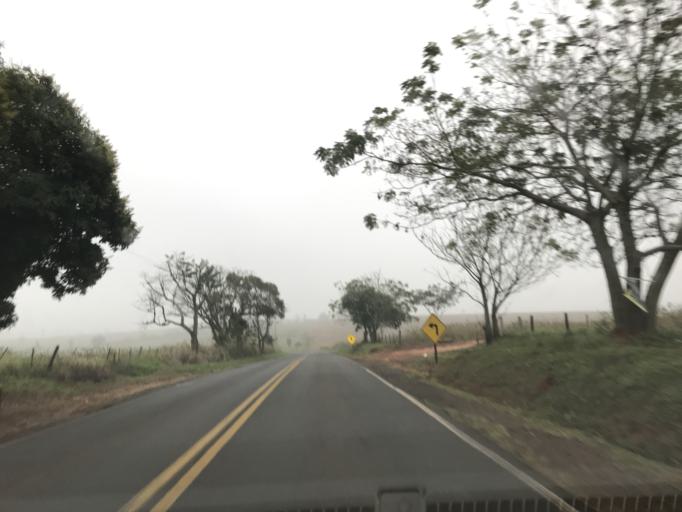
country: PY
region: Canindeyu
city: Salto del Guaira
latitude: -24.0886
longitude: -54.0922
